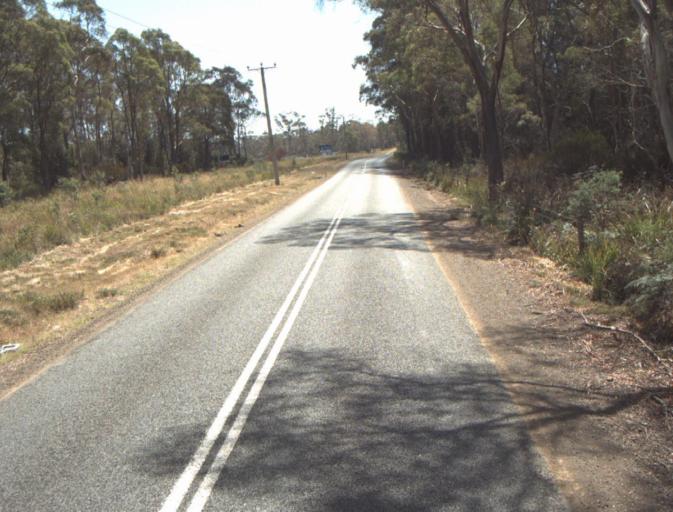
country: AU
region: Tasmania
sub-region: Launceston
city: Mayfield
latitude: -41.3254
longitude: 147.1380
